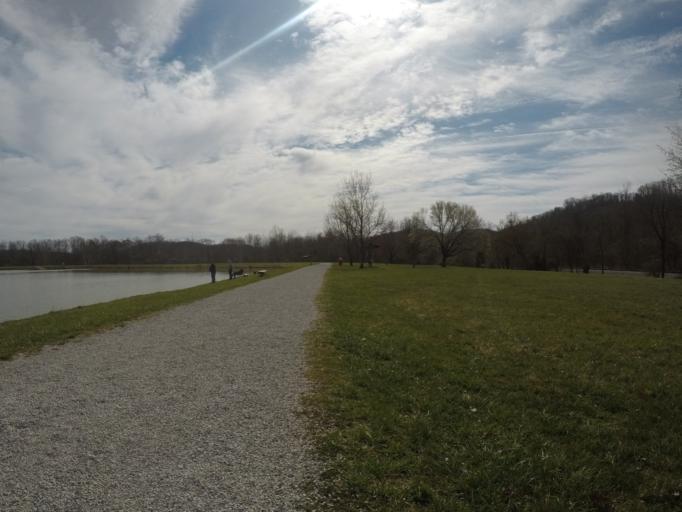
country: US
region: West Virginia
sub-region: Cabell County
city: Barboursville
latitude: 38.3869
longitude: -82.3014
